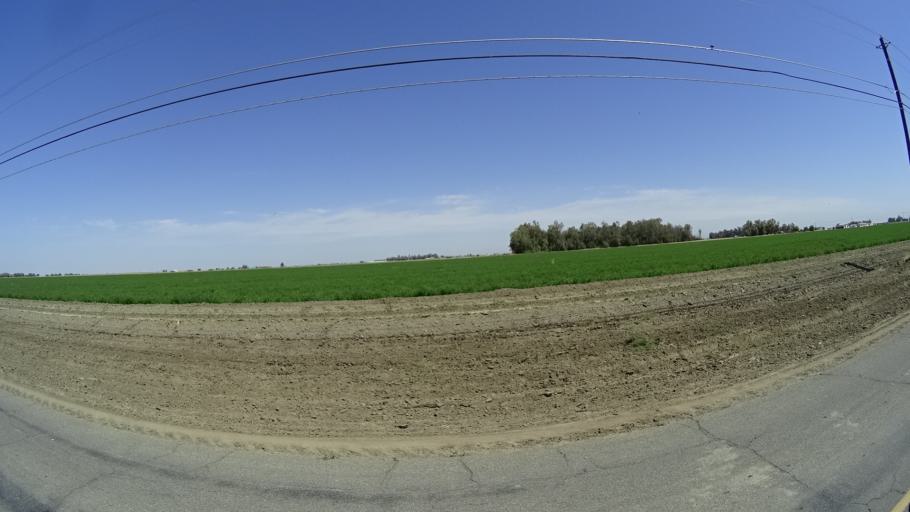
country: US
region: California
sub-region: Kings County
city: Stratford
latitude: 36.1895
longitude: -119.8037
